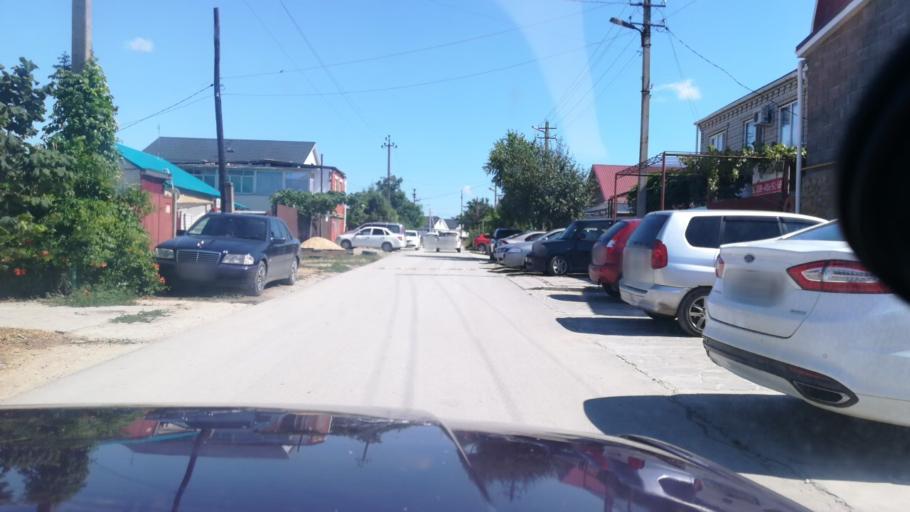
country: RU
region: Krasnodarskiy
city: Vityazevo
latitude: 44.9928
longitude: 37.2744
